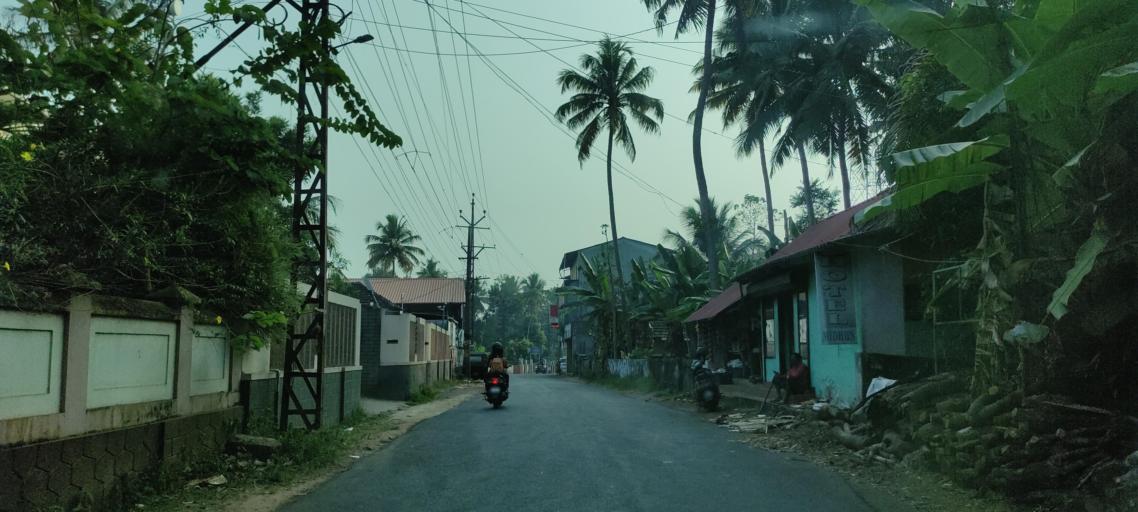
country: IN
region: Kerala
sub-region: Kottayam
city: Vaikam
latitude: 9.7219
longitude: 76.4771
